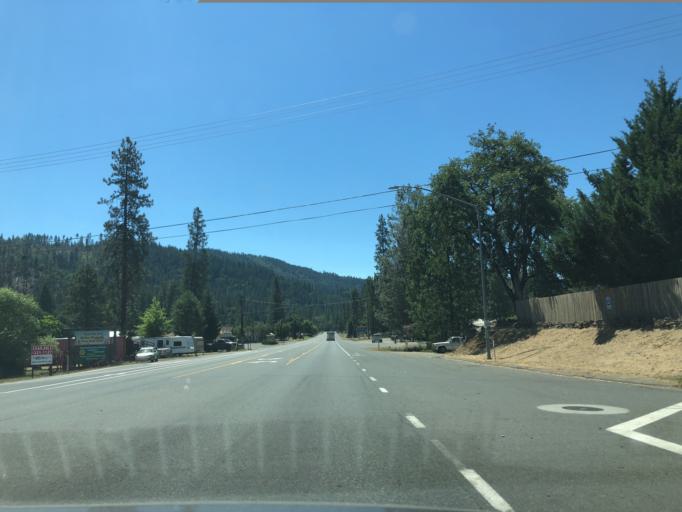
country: US
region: California
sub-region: Trinity County
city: Weaverville
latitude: 40.7206
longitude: -122.9284
